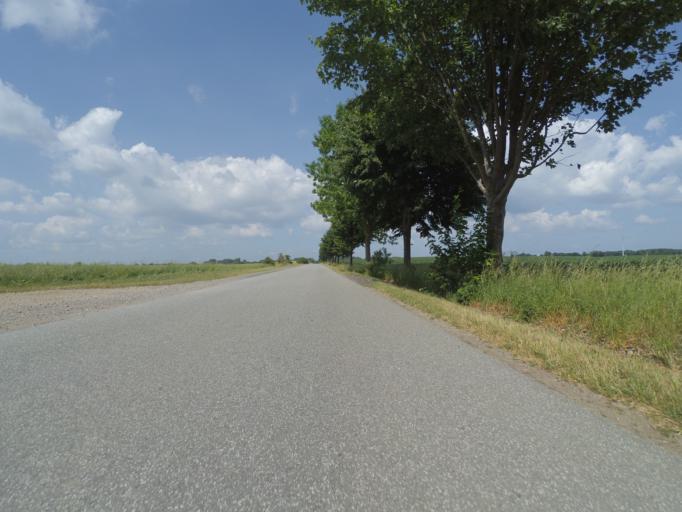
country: DE
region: Mecklenburg-Vorpommern
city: Plau am See
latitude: 53.4480
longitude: 12.2360
